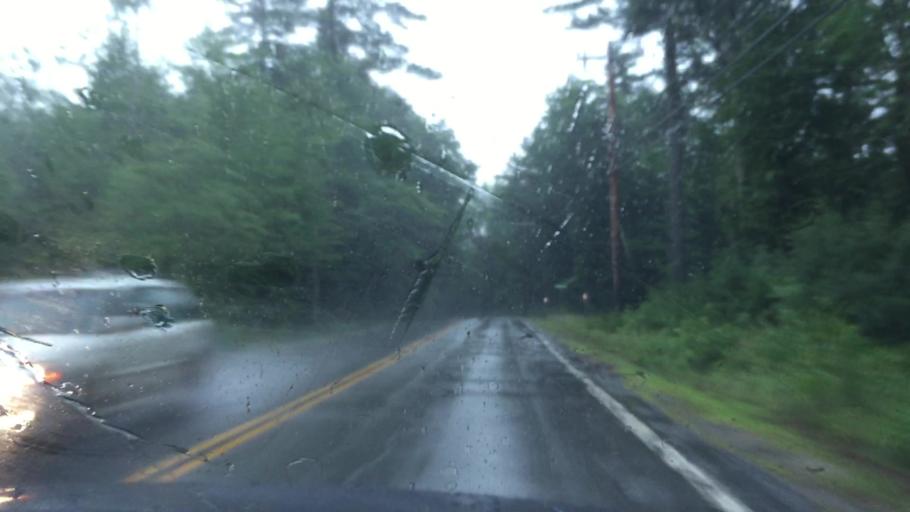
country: US
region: New Hampshire
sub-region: Belknap County
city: Meredith
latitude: 43.6941
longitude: -71.5152
